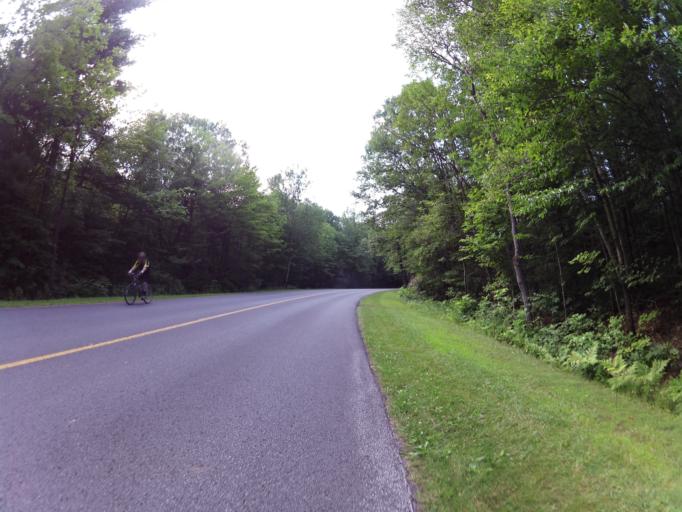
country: CA
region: Quebec
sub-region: Outaouais
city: Gatineau
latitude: 45.4517
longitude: -75.7737
